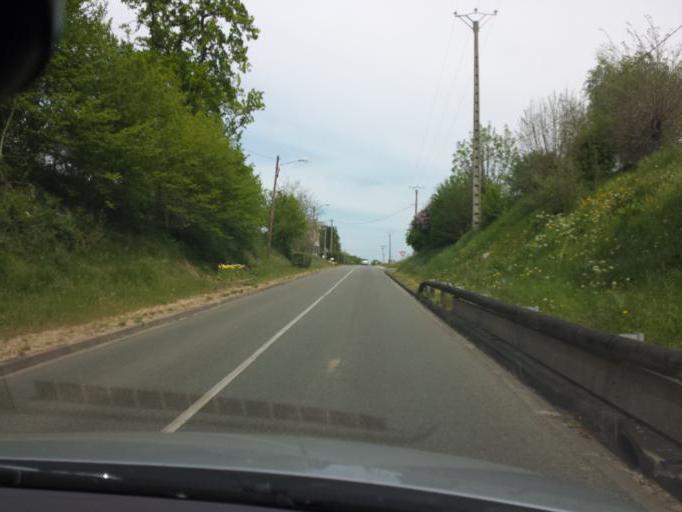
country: FR
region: Ile-de-France
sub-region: Departement des Yvelines
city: Septeuil
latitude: 48.8897
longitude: 1.6839
